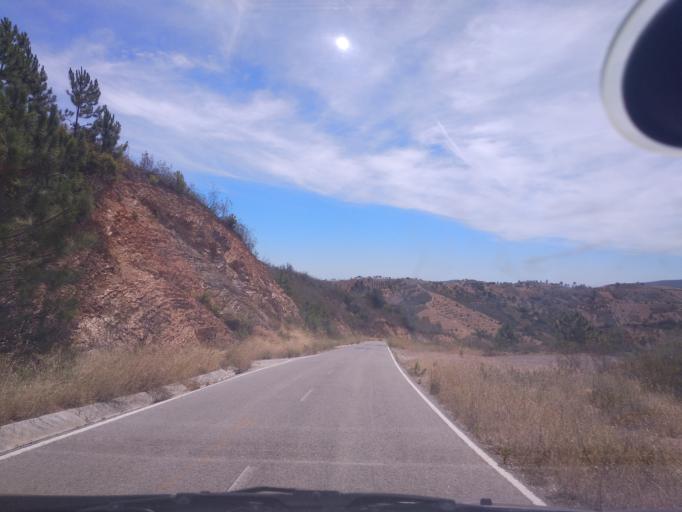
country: PT
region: Faro
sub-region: Sao Bras de Alportel
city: Sao Bras de Alportel
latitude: 37.1867
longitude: -7.7976
